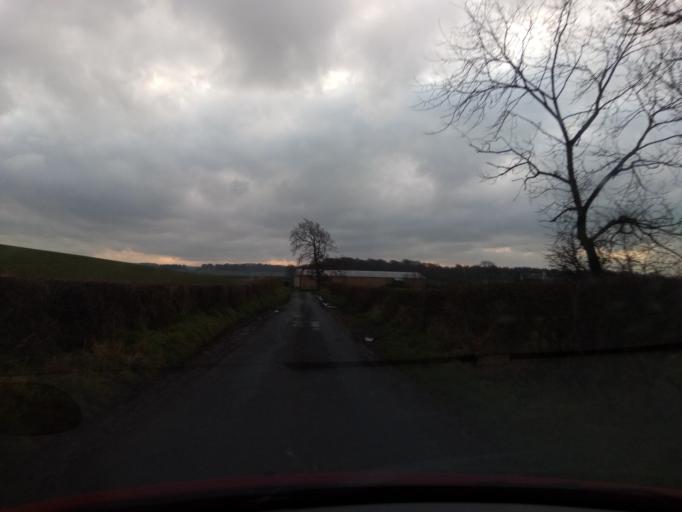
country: GB
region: Scotland
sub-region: The Scottish Borders
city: Newtown St Boswells
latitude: 55.5629
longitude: -2.6814
